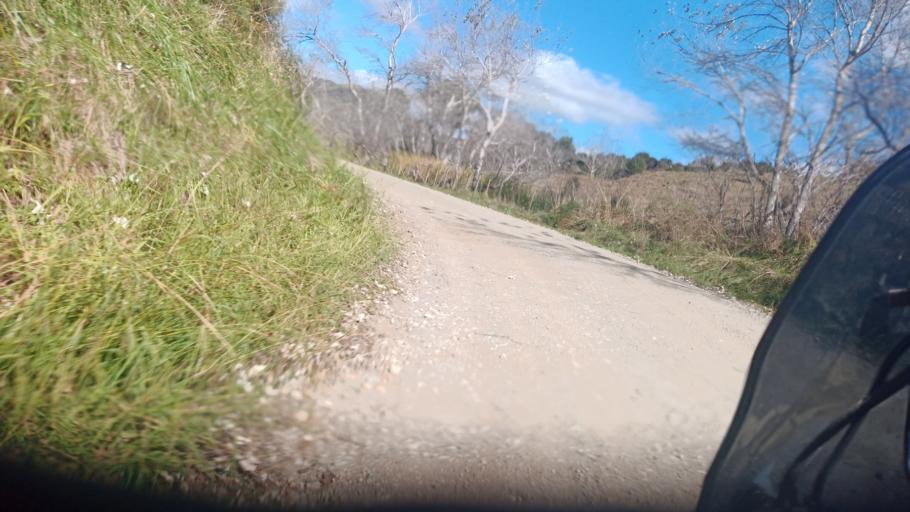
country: NZ
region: Gisborne
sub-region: Gisborne District
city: Gisborne
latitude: -38.3908
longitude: 177.6585
